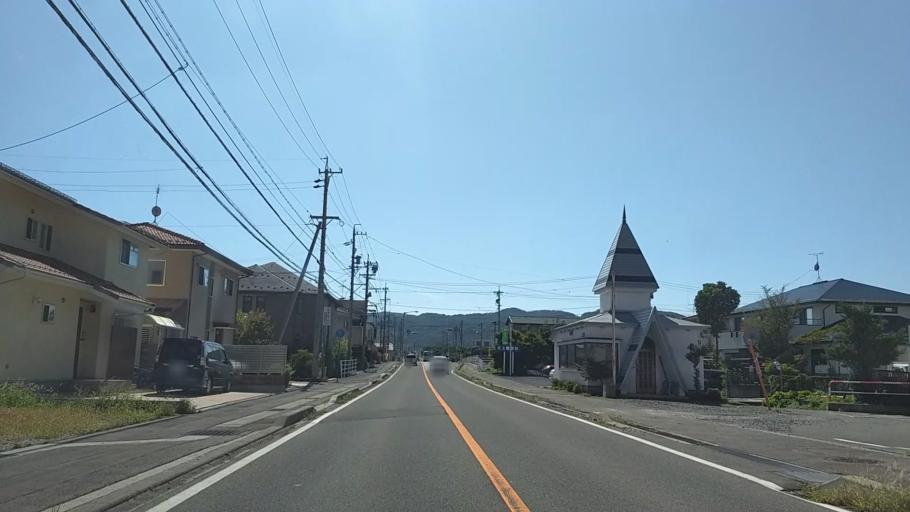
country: JP
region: Nagano
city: Nagano-shi
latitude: 36.6270
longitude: 138.1537
